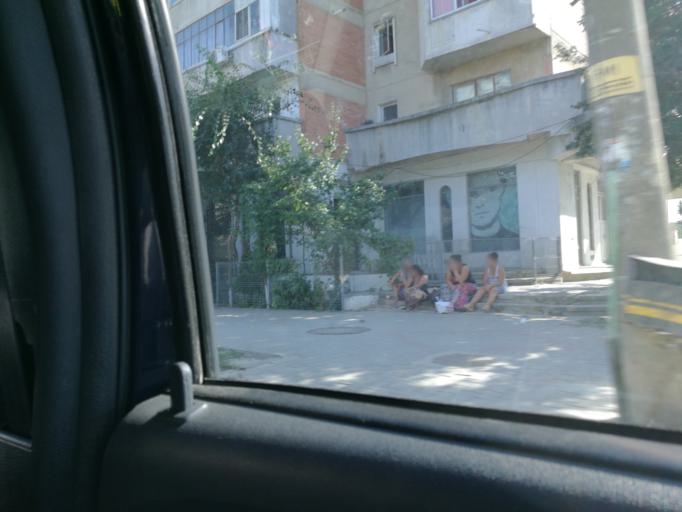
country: RO
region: Iasi
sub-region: Municipiul Iasi
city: Iasi
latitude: 47.1711
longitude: 27.5610
